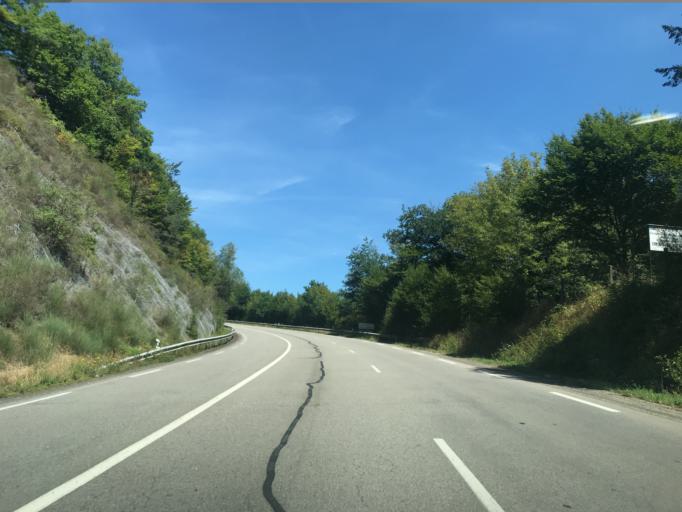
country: FR
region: Limousin
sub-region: Departement de la Correze
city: Tulle
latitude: 45.2653
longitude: 1.7910
